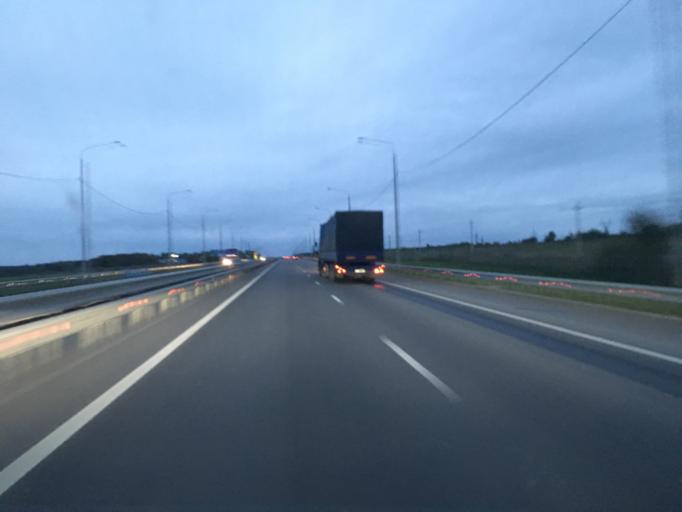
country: RU
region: Kaluga
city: Maloyaroslavets
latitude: 54.9509
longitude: 36.4470
